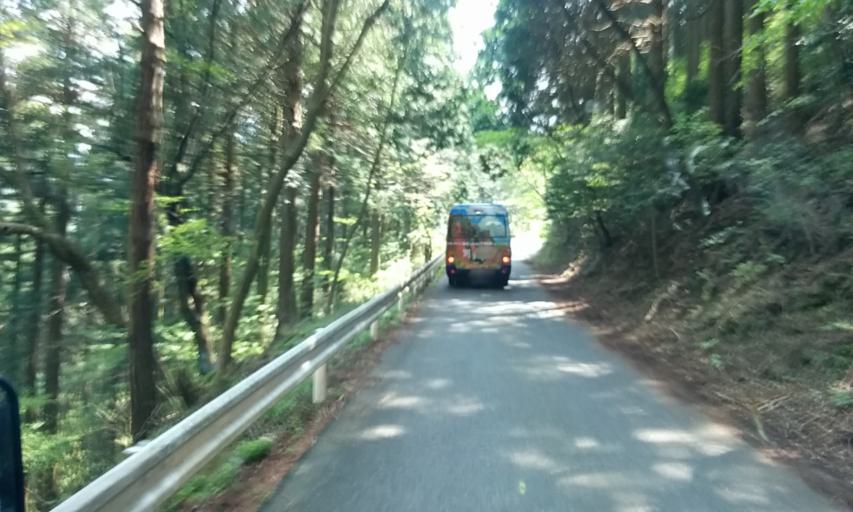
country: JP
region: Ehime
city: Niihama
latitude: 33.8766
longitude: 133.2970
